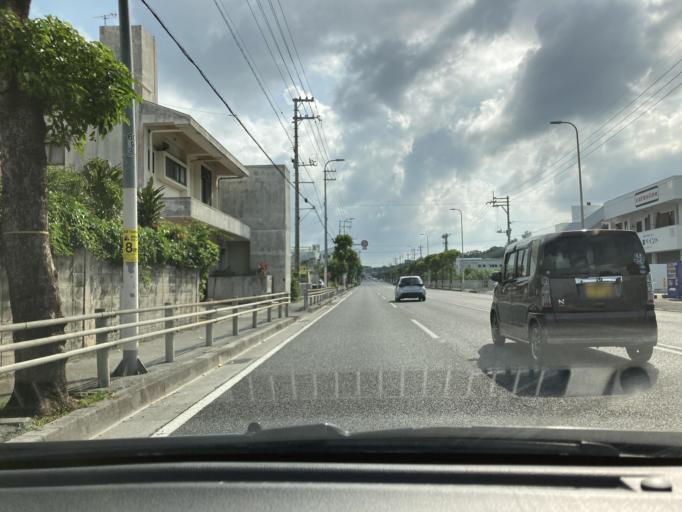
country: JP
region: Okinawa
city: Ginowan
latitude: 26.2441
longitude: 127.7806
